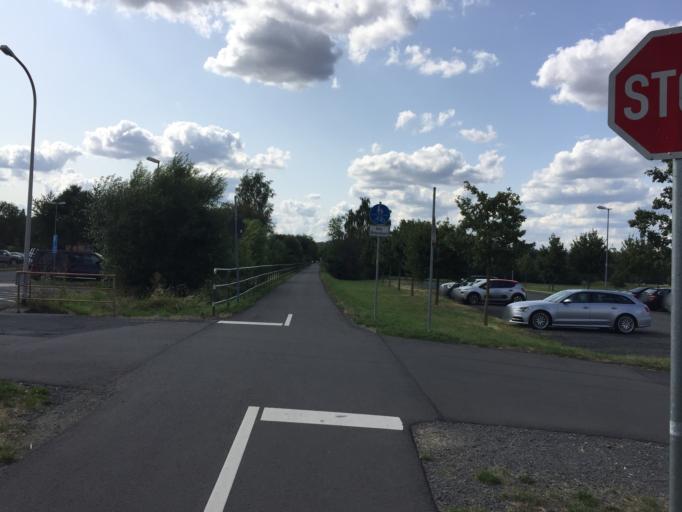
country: DE
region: Hesse
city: Schwalmstadt
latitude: 50.9101
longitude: 9.2032
